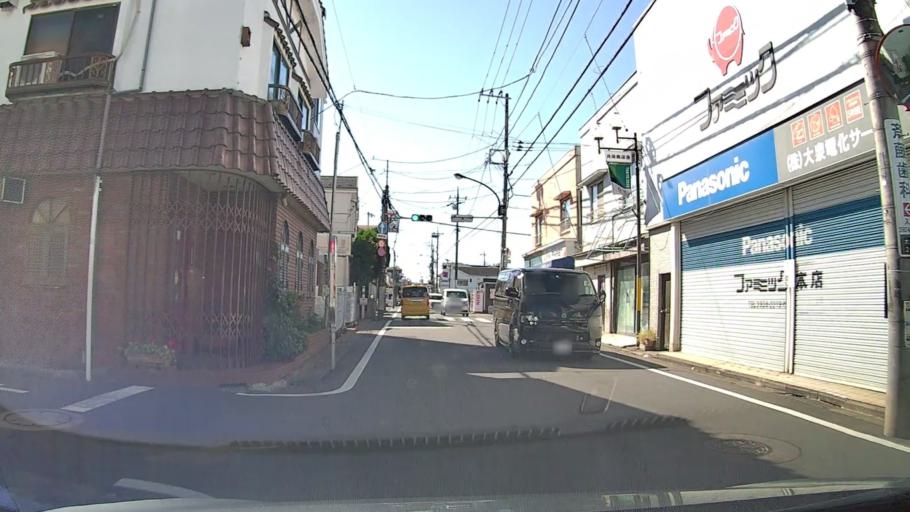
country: JP
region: Saitama
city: Wako
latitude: 35.7611
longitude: 139.6067
